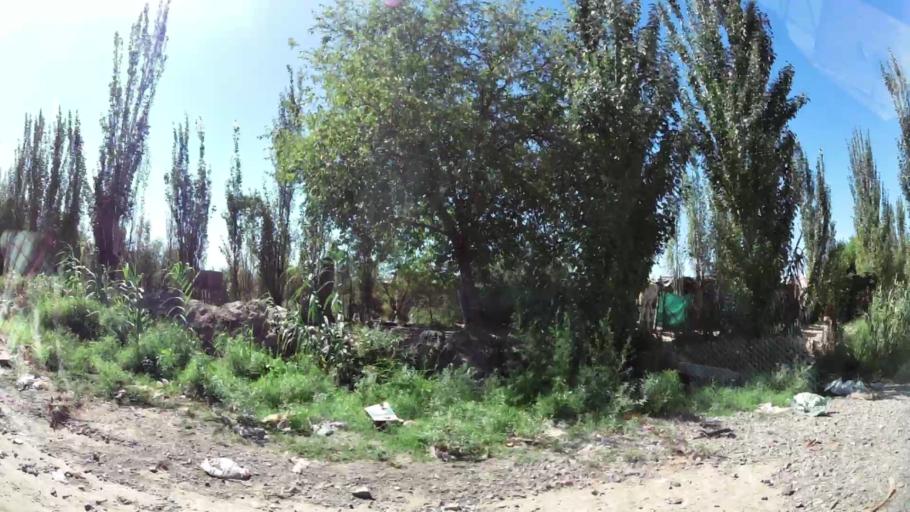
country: AR
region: Mendoza
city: Las Heras
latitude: -32.8247
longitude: -68.8251
